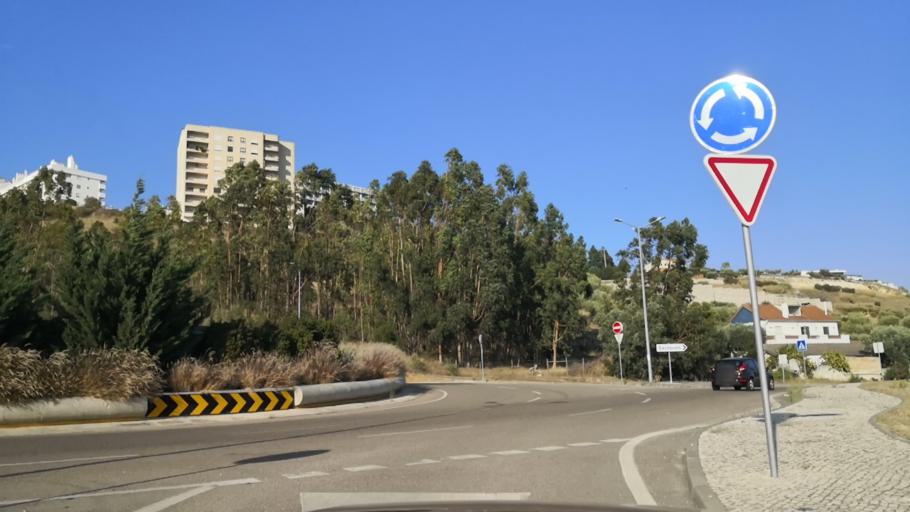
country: PT
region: Santarem
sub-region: Santarem
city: Santarem
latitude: 39.2212
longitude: -8.6946
